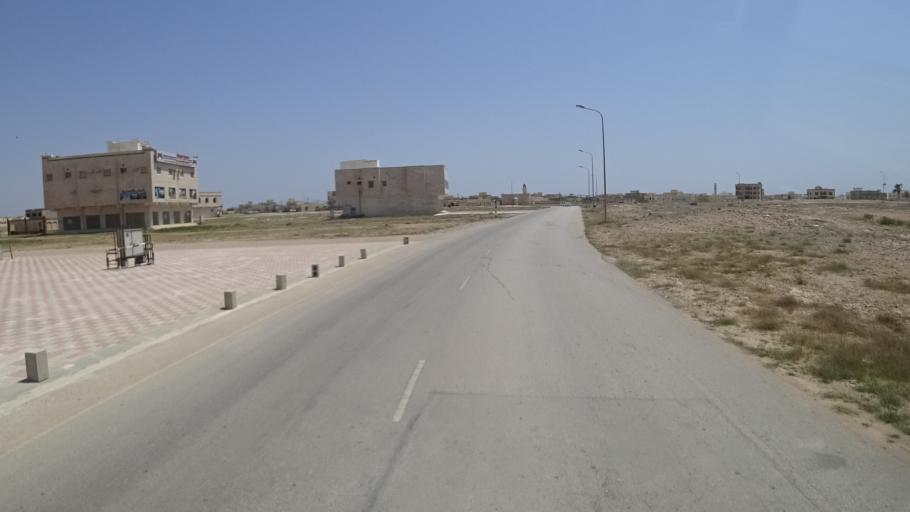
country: OM
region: Zufar
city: Salalah
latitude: 16.9956
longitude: 54.6965
